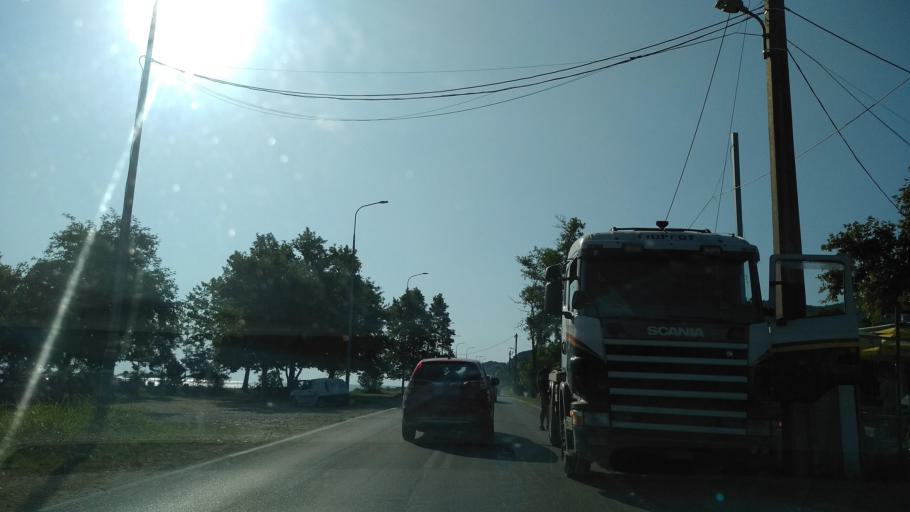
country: GR
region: Central Macedonia
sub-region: Nomos Thessalonikis
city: Stavros
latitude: 40.6618
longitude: 23.7198
